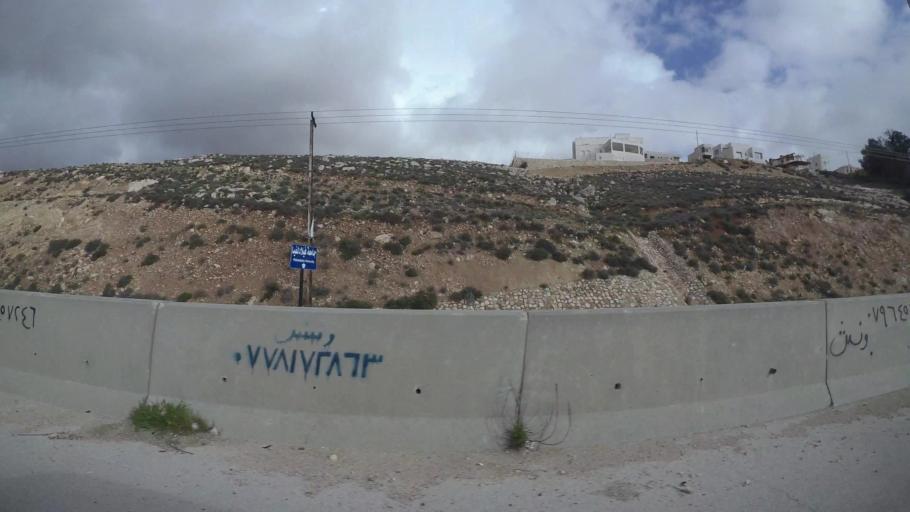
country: JO
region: Amman
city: Al Jubayhah
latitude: 32.0745
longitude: 35.8785
